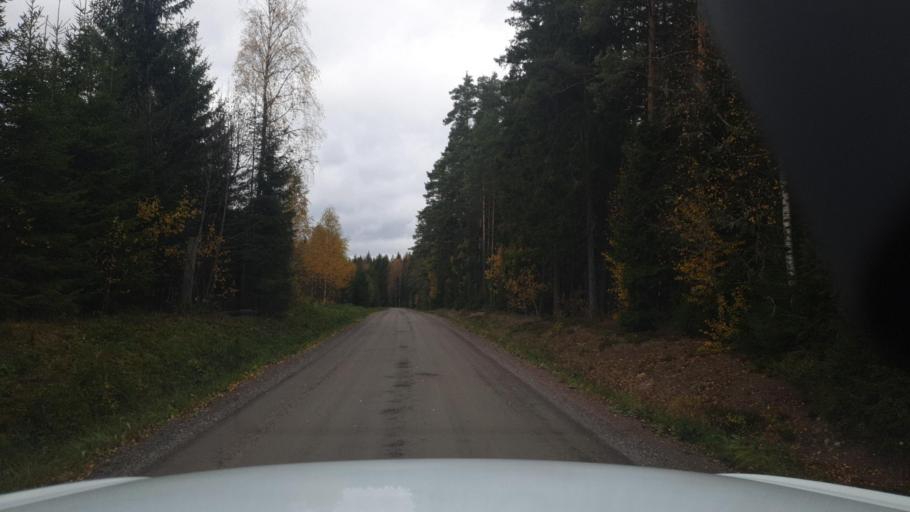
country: SE
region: Vaermland
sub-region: Sunne Kommun
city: Sunne
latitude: 59.8057
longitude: 13.0803
